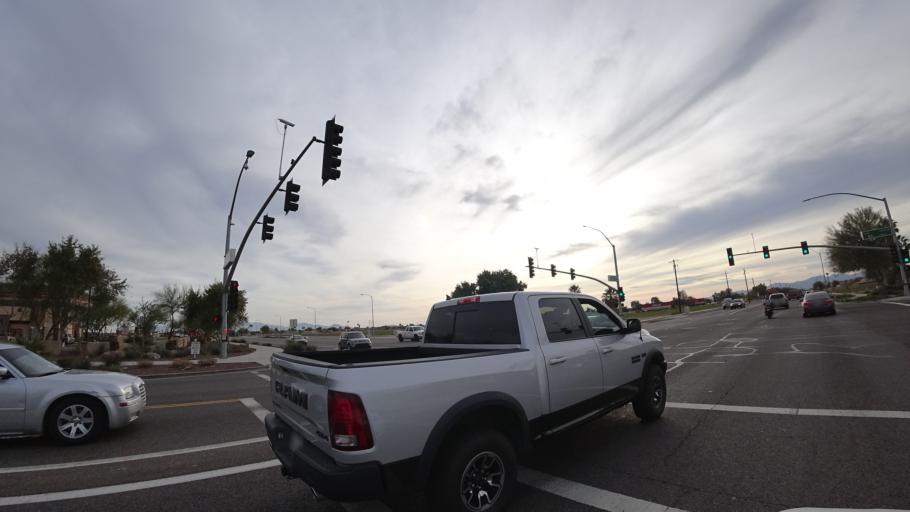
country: US
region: Arizona
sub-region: Maricopa County
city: Peoria
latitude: 33.5666
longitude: -112.2374
